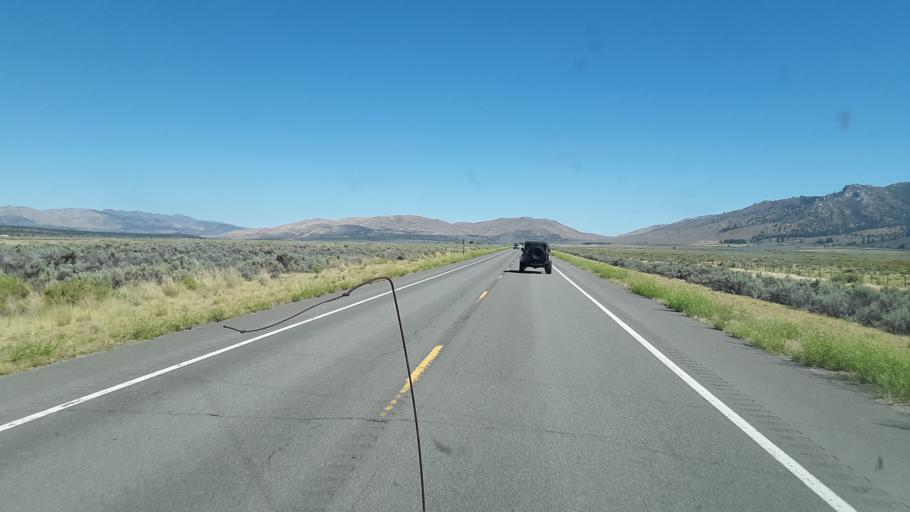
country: US
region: Nevada
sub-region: Washoe County
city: Cold Springs
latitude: 39.9916
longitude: -120.0747
